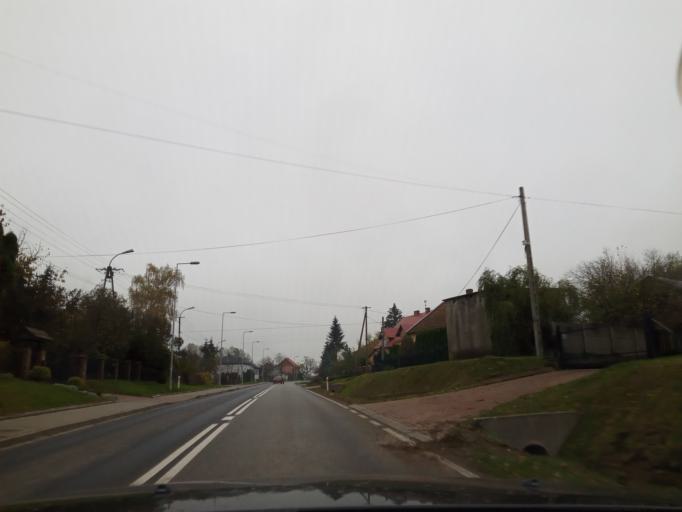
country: PL
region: Lesser Poland Voivodeship
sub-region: Powiat proszowicki
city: Klimontow
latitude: 50.2311
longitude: 20.3660
